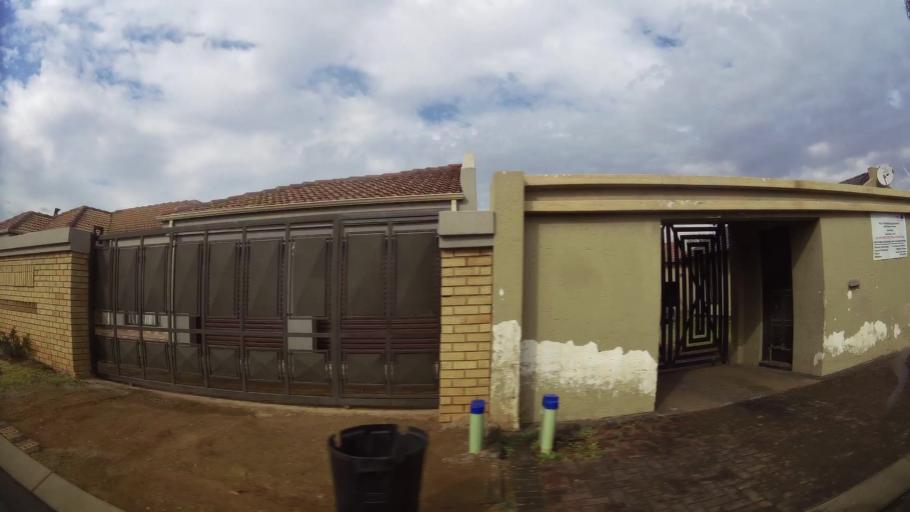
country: ZA
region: Gauteng
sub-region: Ekurhuleni Metropolitan Municipality
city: Germiston
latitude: -26.3218
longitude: 28.1765
